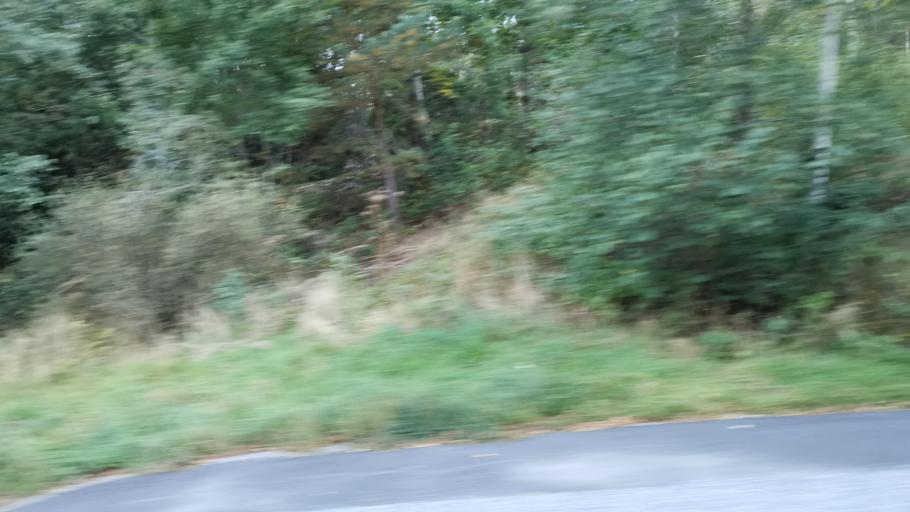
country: SE
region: Vaestra Goetaland
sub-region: Tanums Kommun
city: Tanumshede
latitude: 58.6972
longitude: 11.3380
